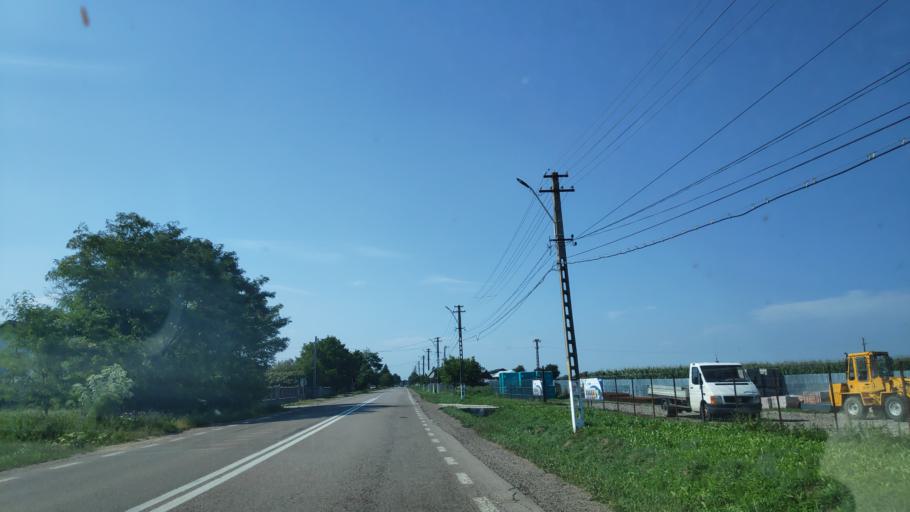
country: RO
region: Suceava
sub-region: Comuna Boroaia
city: Boroaia
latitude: 47.3585
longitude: 26.3438
